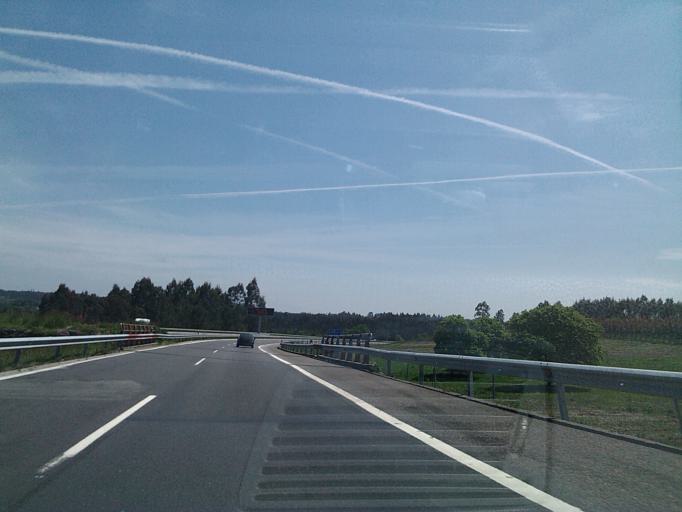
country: ES
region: Galicia
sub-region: Provincia da Coruna
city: Oroso
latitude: 42.9102
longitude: -8.4484
